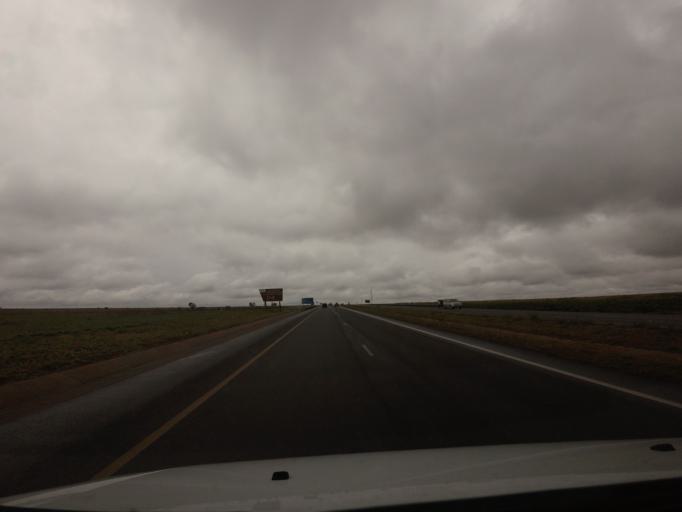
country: ZA
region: Mpumalanga
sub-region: Nkangala District Municipality
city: Middelburg
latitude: -25.8299
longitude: 29.5149
